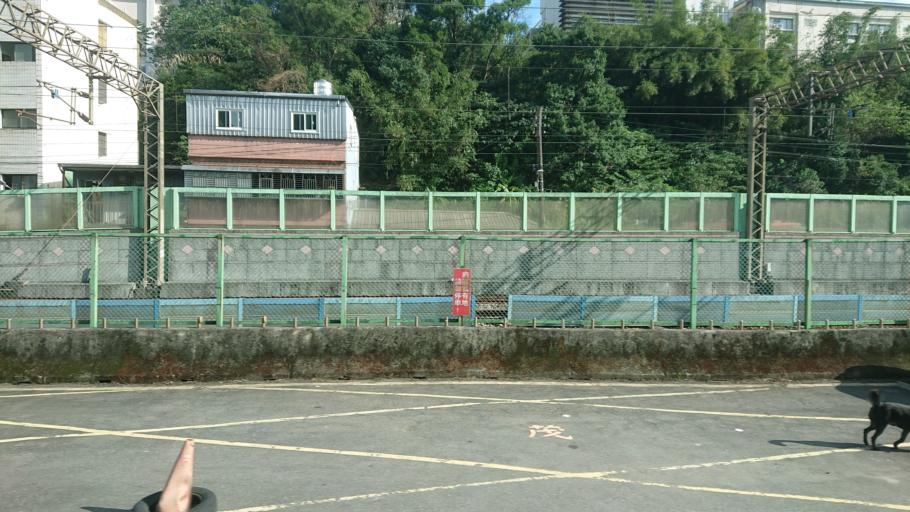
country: TW
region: Taiwan
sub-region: Keelung
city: Keelung
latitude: 25.1100
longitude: 121.8022
